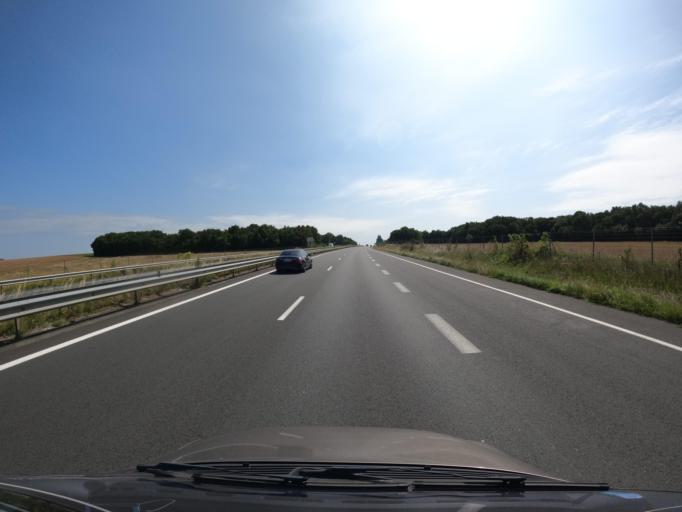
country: FR
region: Poitou-Charentes
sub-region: Departement des Deux-Sevres
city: Saint-Hilaire-la-Palud
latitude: 46.2107
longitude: -0.7445
